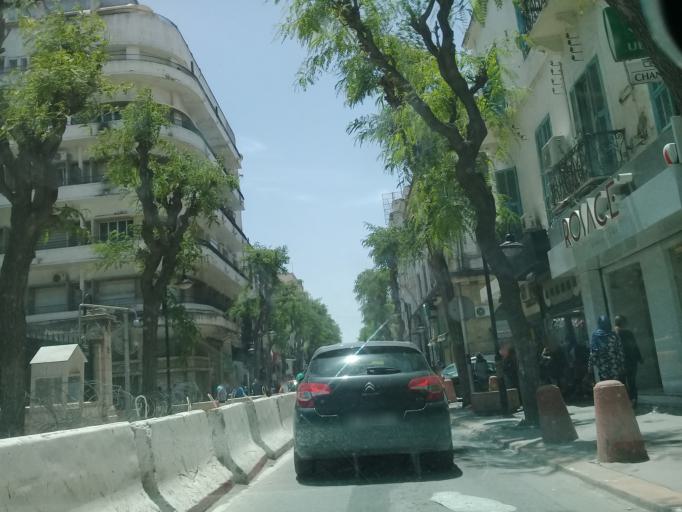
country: TN
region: Tunis
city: Tunis
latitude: 36.7984
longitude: 10.1787
